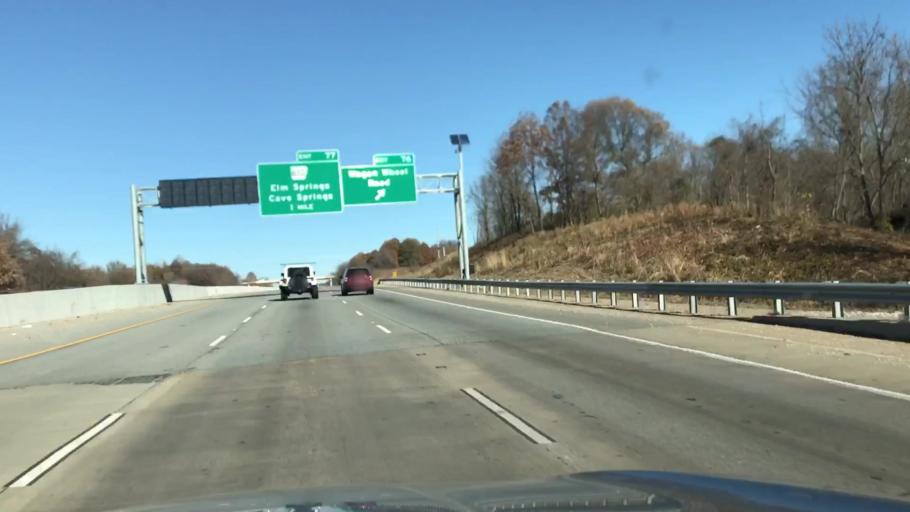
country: US
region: Arkansas
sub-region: Benton County
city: Bethel Heights
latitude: 36.2209
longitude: -94.1802
